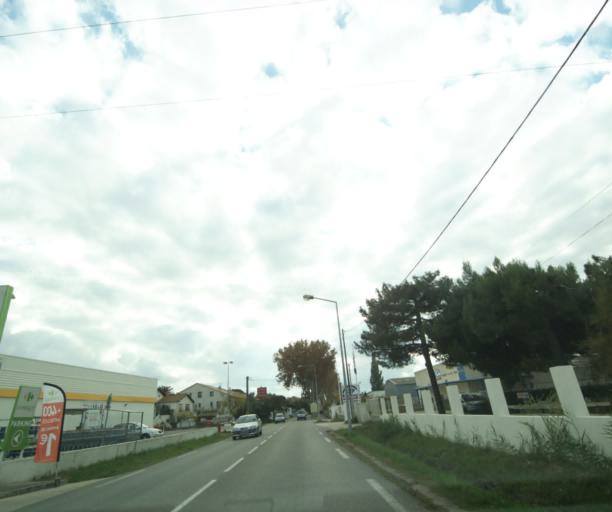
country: FR
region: Languedoc-Roussillon
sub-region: Departement du Gard
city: Aigues-Mortes
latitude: 43.5739
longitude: 4.1955
